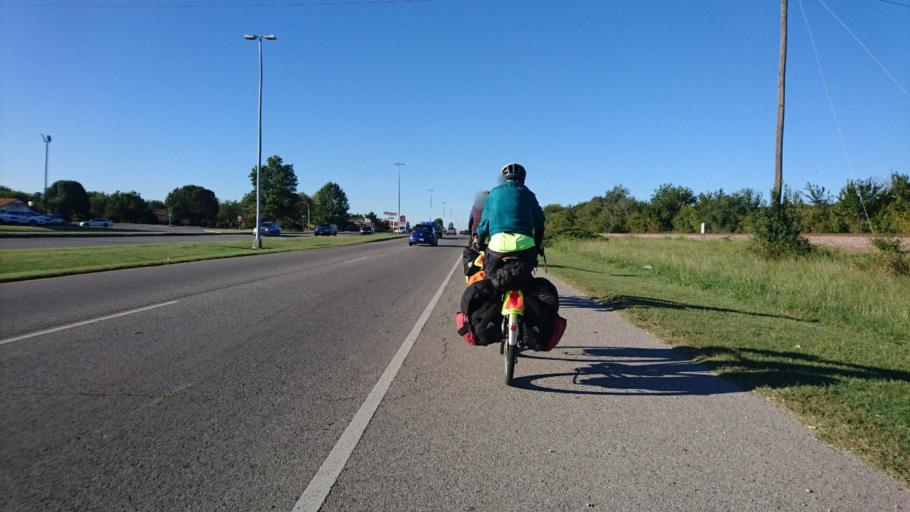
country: US
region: Oklahoma
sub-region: Rogers County
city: Claremore
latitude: 36.3039
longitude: -95.6236
